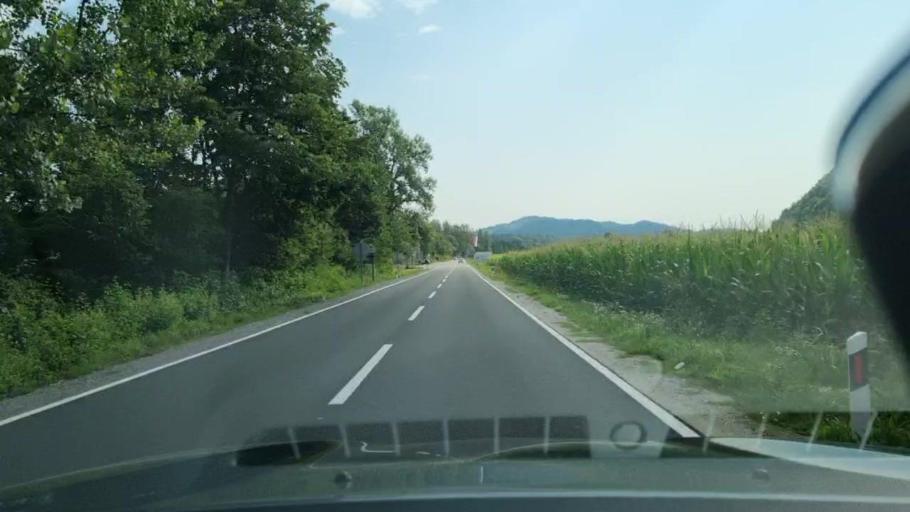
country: BA
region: Federation of Bosnia and Herzegovina
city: Otoka
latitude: 44.9823
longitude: 16.2086
